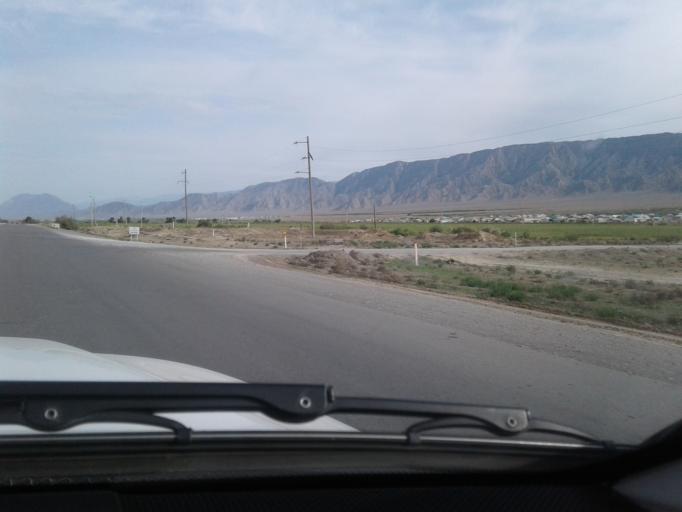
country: TM
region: Ahal
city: Arcabil
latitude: 38.2099
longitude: 57.8140
